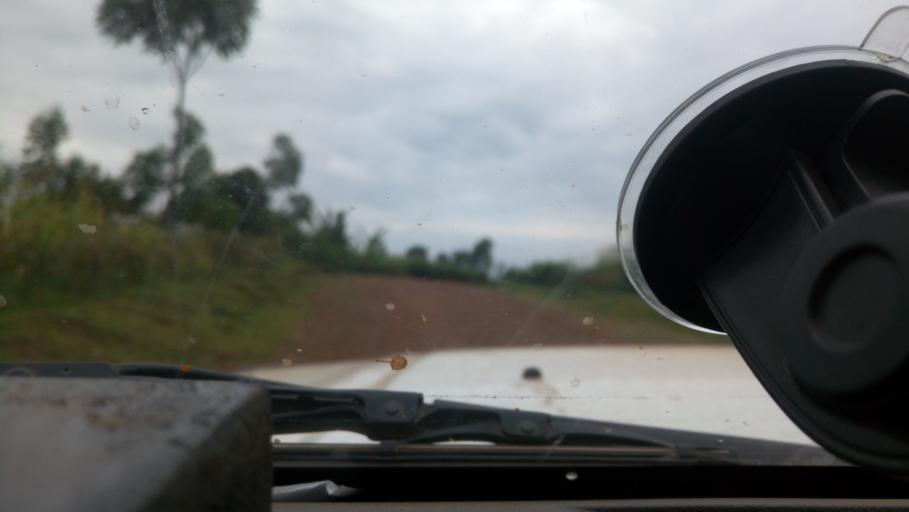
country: KE
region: Kisii
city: Ogembo
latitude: -0.8481
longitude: 34.6086
